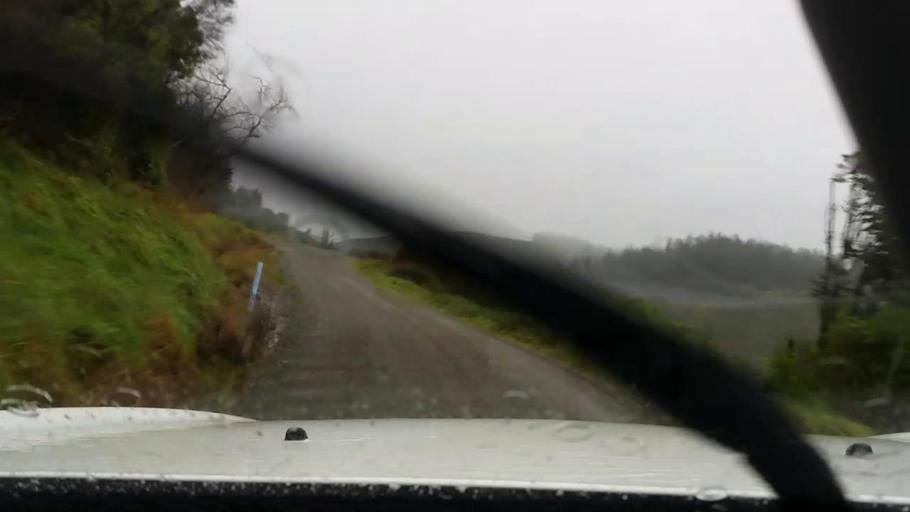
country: NZ
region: Wellington
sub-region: Masterton District
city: Masterton
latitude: -41.1828
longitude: 175.8244
